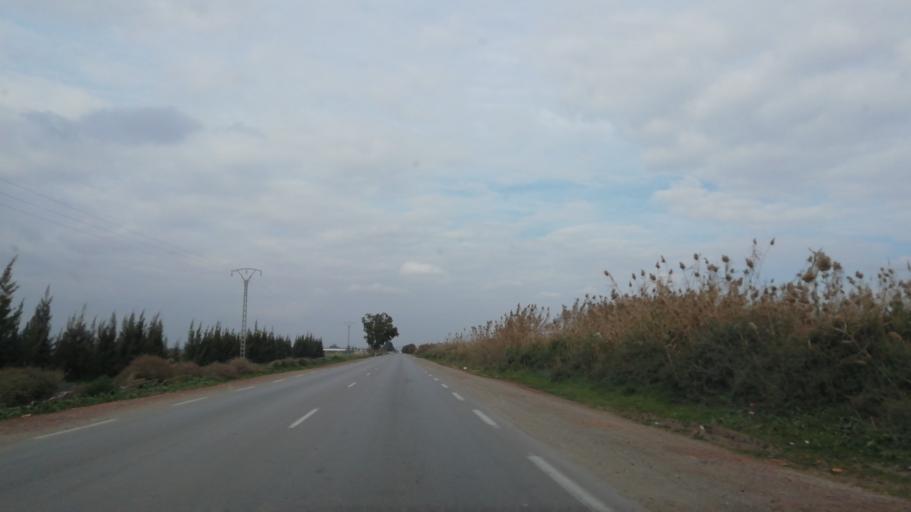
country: DZ
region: Mascara
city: Mascara
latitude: 35.6444
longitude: 0.0601
